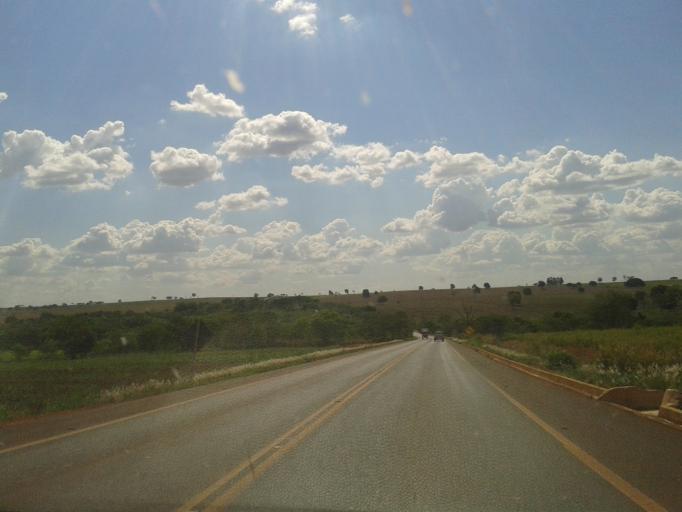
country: BR
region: Minas Gerais
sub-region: Centralina
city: Centralina
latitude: -18.6904
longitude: -49.3654
